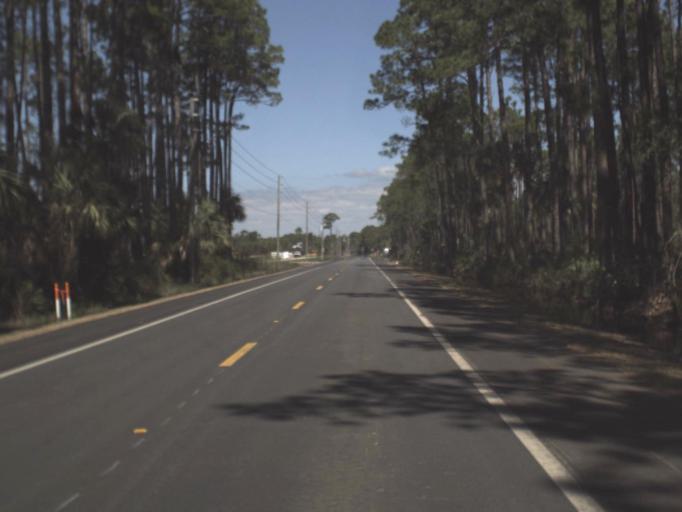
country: US
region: Florida
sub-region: Gulf County
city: Port Saint Joe
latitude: 29.7325
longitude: -85.3021
